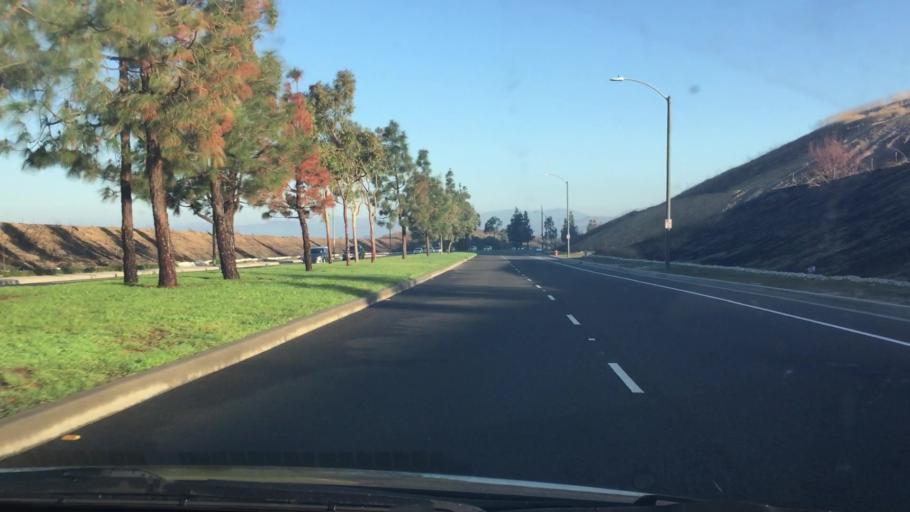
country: US
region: California
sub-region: Orange County
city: North Tustin
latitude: 33.7761
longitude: -117.7591
